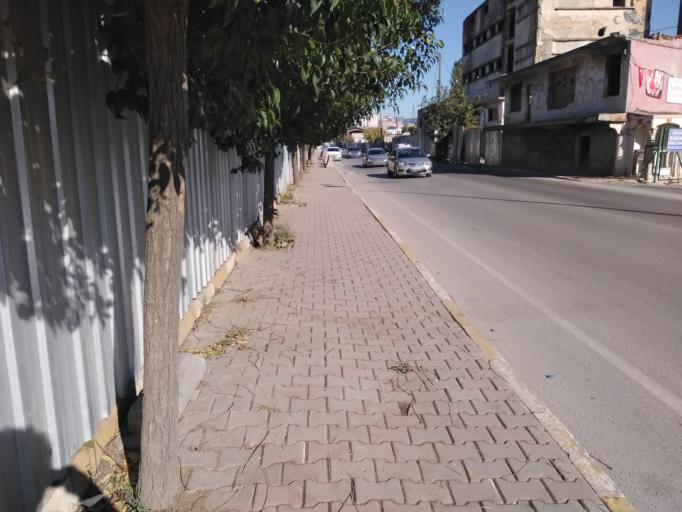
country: TR
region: Istanbul
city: Maltepe
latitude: 40.9131
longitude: 29.1359
